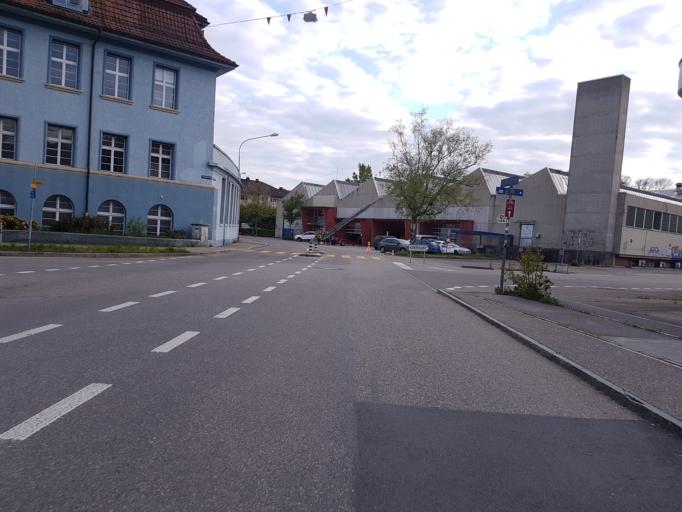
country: CH
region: Bern
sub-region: Biel/Bienne District
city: Nidau
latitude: 47.1272
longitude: 7.2371
